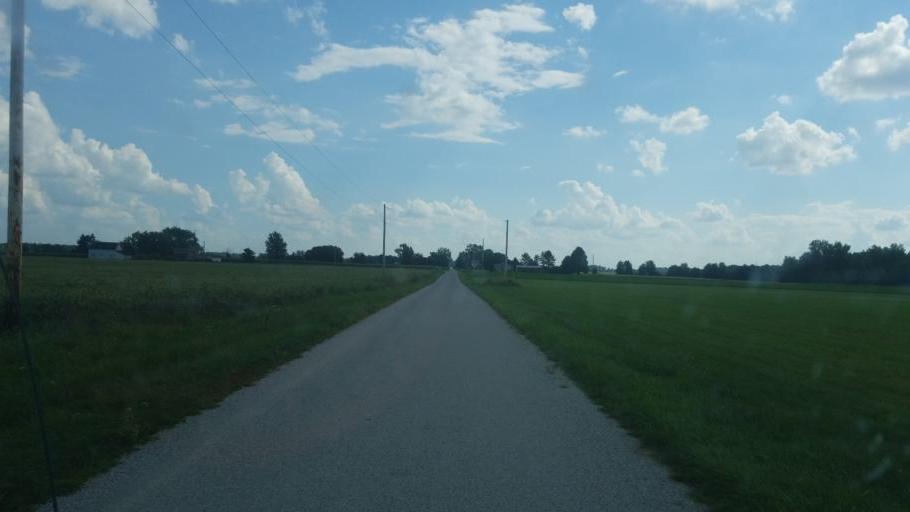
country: US
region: Ohio
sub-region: Huron County
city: Willard
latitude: 40.9849
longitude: -82.8160
